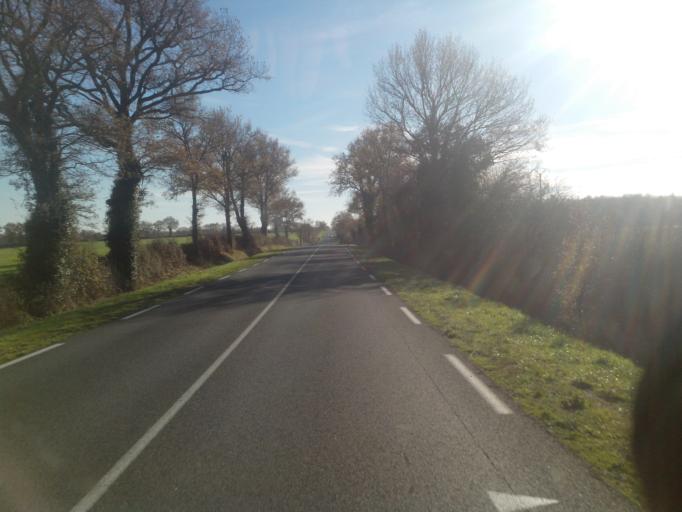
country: FR
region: Limousin
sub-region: Departement de la Haute-Vienne
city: Bussiere-Poitevine
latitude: 46.2952
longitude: 0.8422
